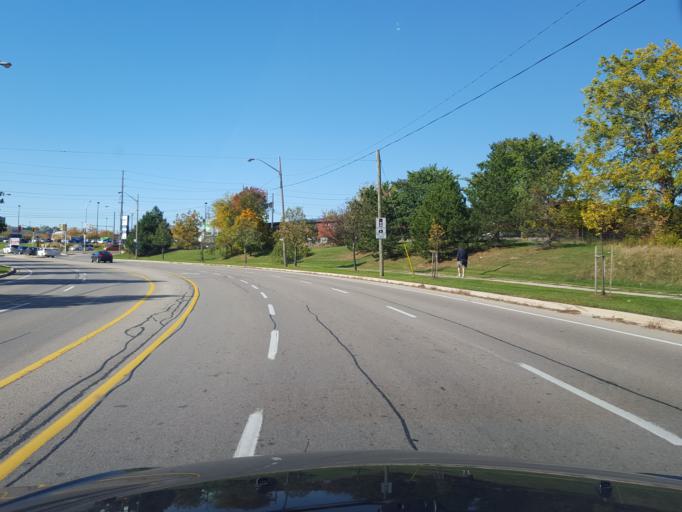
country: CA
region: Ontario
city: Burlington
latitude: 43.3450
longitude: -79.8240
